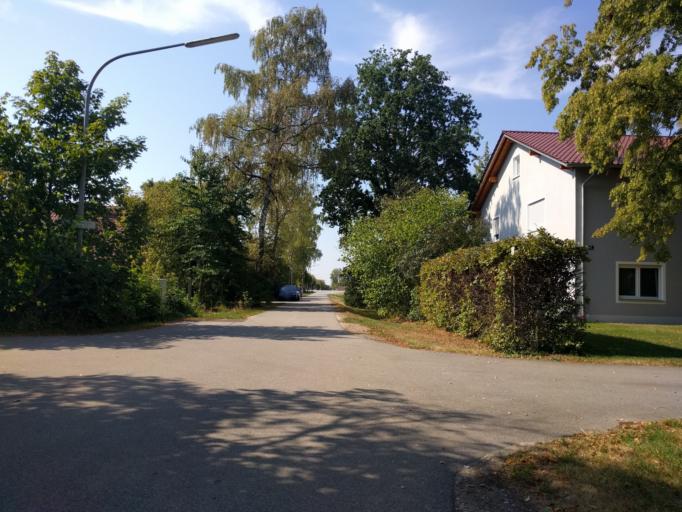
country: DE
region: Bavaria
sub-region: Upper Palatinate
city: Mintraching
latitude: 48.9867
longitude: 12.2559
